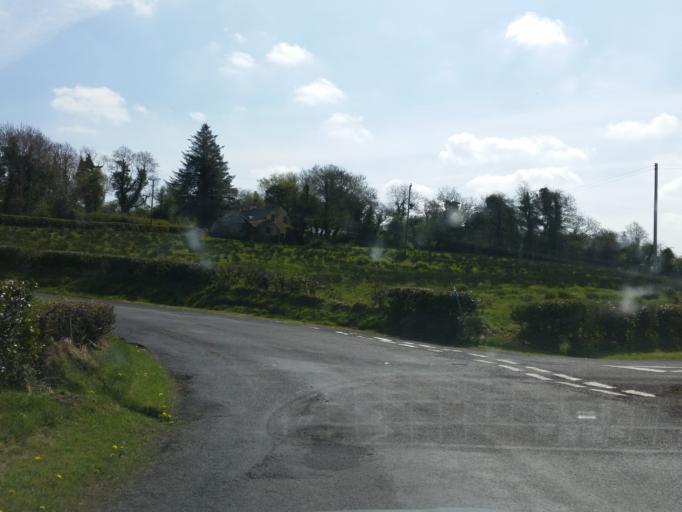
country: GB
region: Northern Ireland
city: Fivemiletown
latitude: 54.3090
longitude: -7.3584
